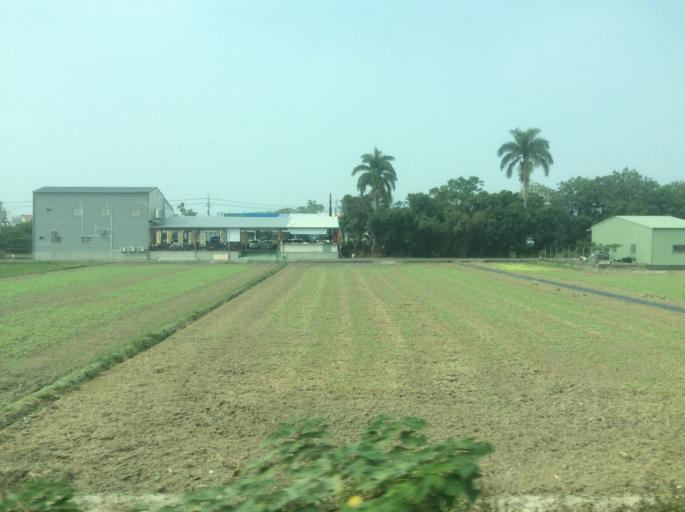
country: TW
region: Taiwan
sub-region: Chiayi
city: Jiayi Shi
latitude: 23.4459
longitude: 120.4104
